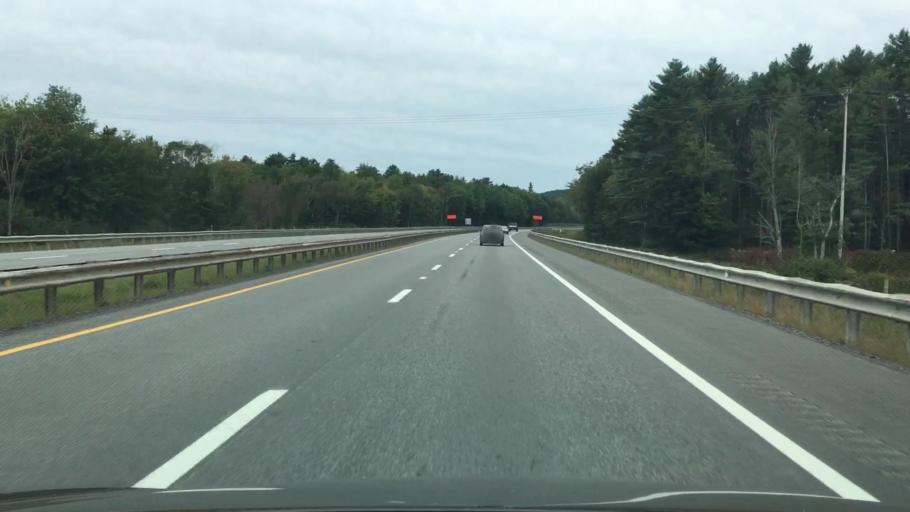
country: US
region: Maine
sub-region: Androscoggin County
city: Lisbon
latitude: 44.0694
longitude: -70.1420
